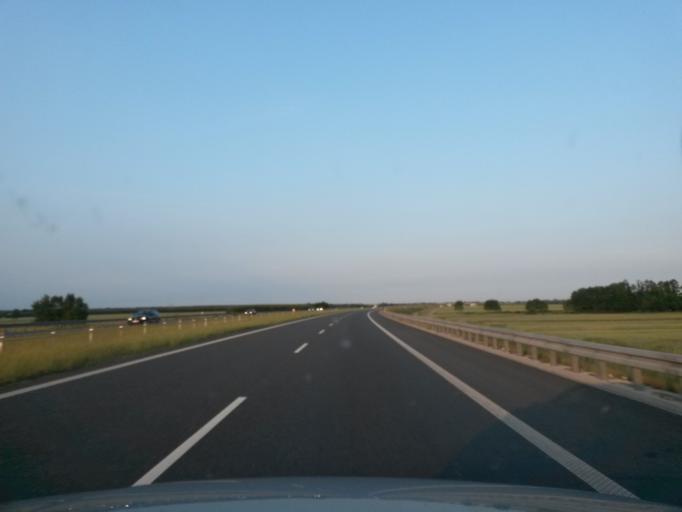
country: PL
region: Lodz Voivodeship
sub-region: Powiat wieruszowski
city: Sokolniki
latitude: 51.3236
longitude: 18.3271
